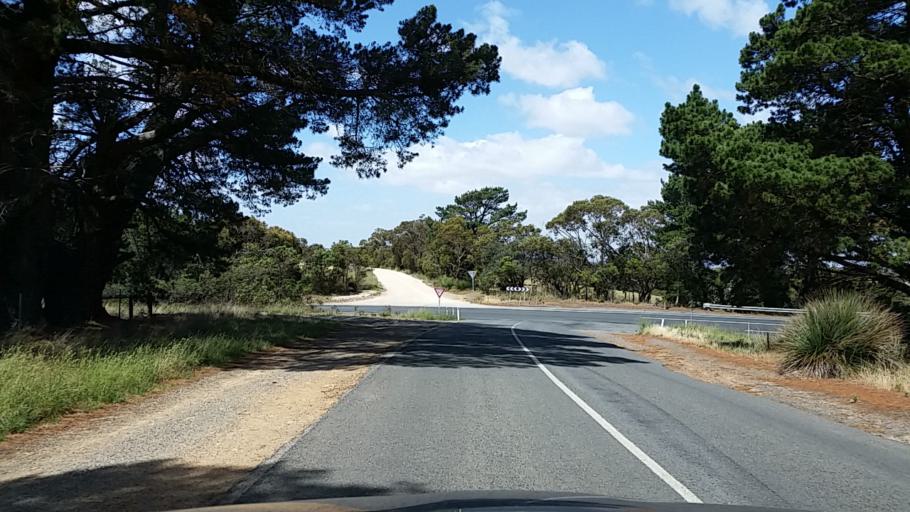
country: AU
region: South Australia
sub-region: Alexandrina
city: Port Elliot
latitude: -35.4540
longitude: 138.6431
